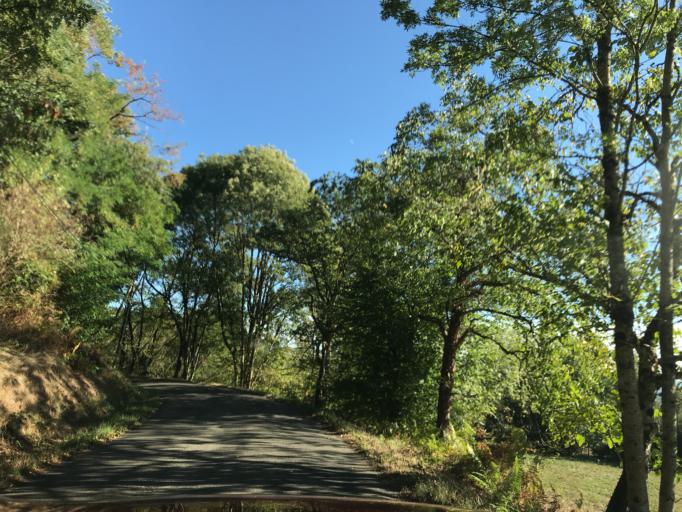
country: FR
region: Auvergne
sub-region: Departement du Puy-de-Dome
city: Escoutoux
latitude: 45.7768
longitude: 3.6082
